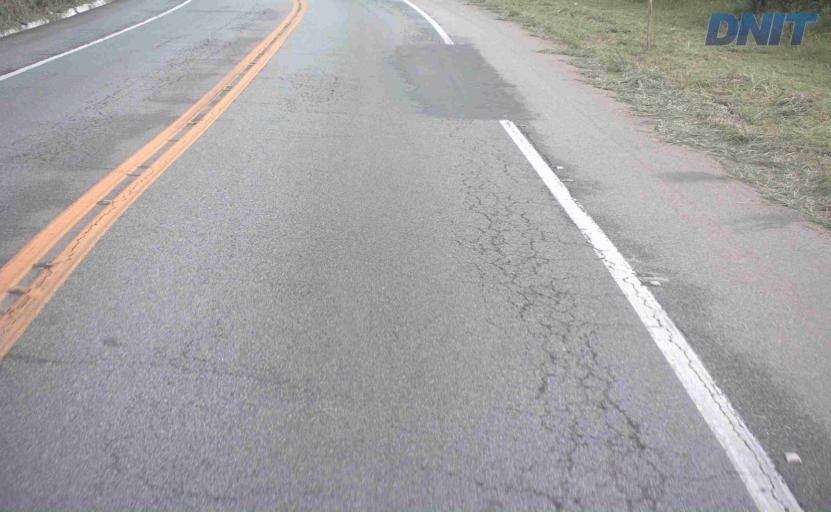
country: BR
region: Minas Gerais
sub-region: Joao Monlevade
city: Joao Monlevade
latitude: -19.8544
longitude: -43.2601
